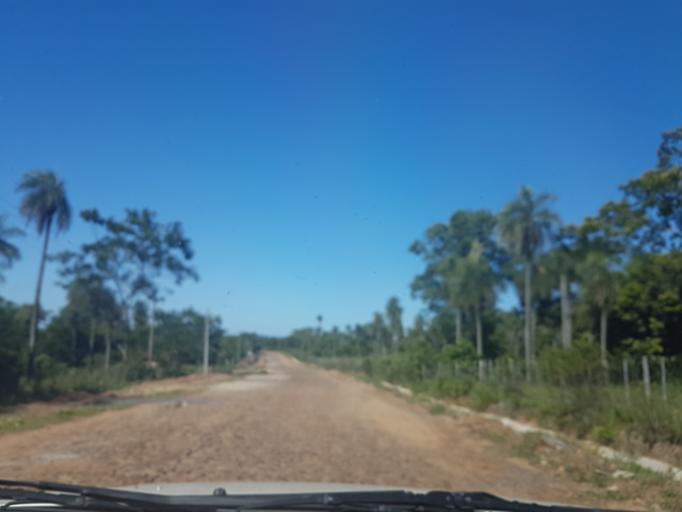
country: PY
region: Cordillera
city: Atyra
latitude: -25.2774
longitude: -57.1421
